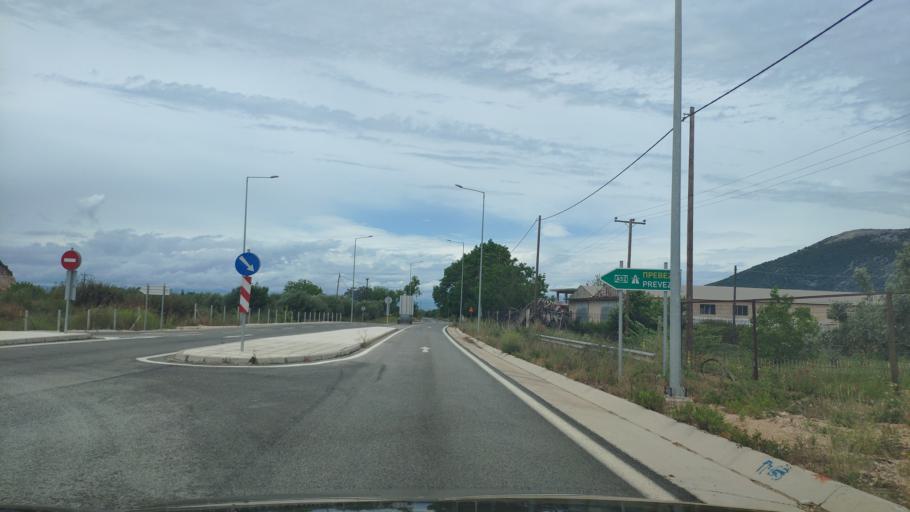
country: GR
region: West Greece
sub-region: Nomos Aitolias kai Akarnanias
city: Vonitsa
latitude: 38.8928
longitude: 20.8999
